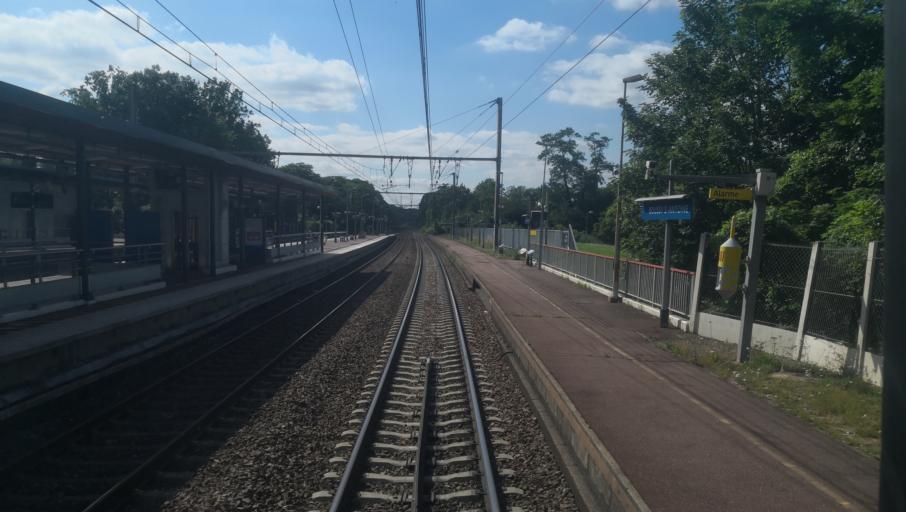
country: FR
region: Ile-de-France
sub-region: Departement de l'Essonne
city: Quincy-sous-Senart
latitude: 48.6809
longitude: 2.5335
